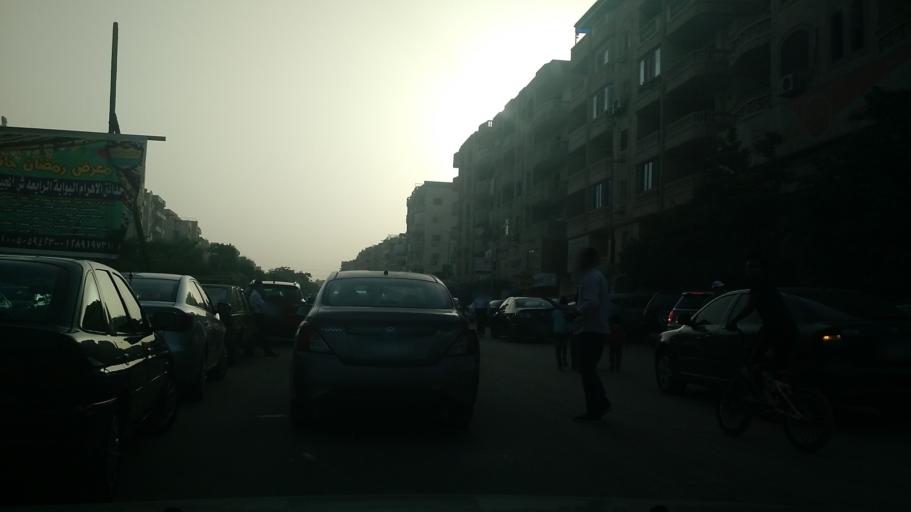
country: EG
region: Al Jizah
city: Al Jizah
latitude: 29.9812
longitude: 31.1090
